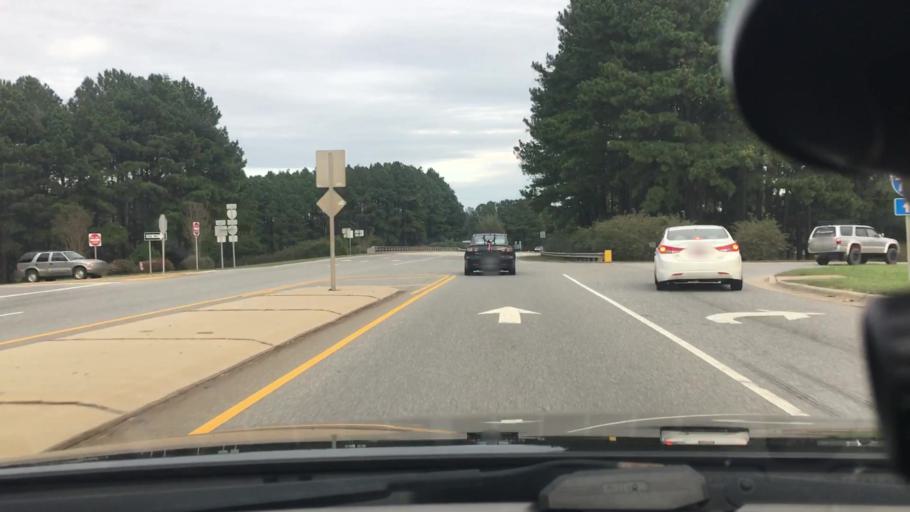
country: US
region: North Carolina
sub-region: Montgomery County
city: Biscoe
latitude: 35.3608
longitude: -79.7671
